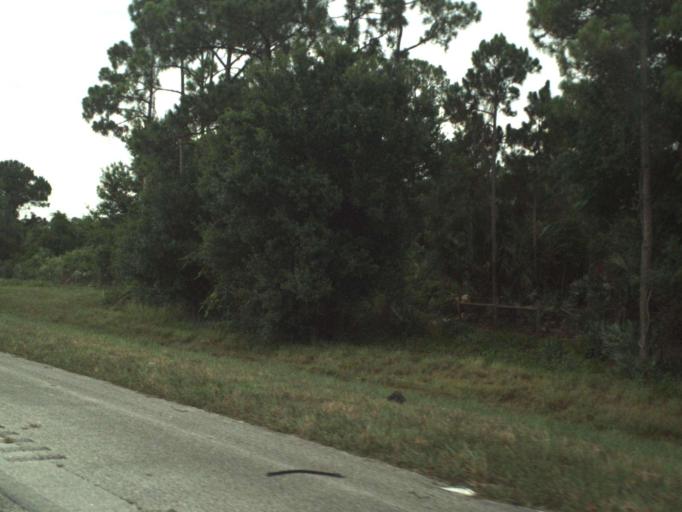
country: US
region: Florida
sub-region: Martin County
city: Palm City
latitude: 27.1286
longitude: -80.3474
